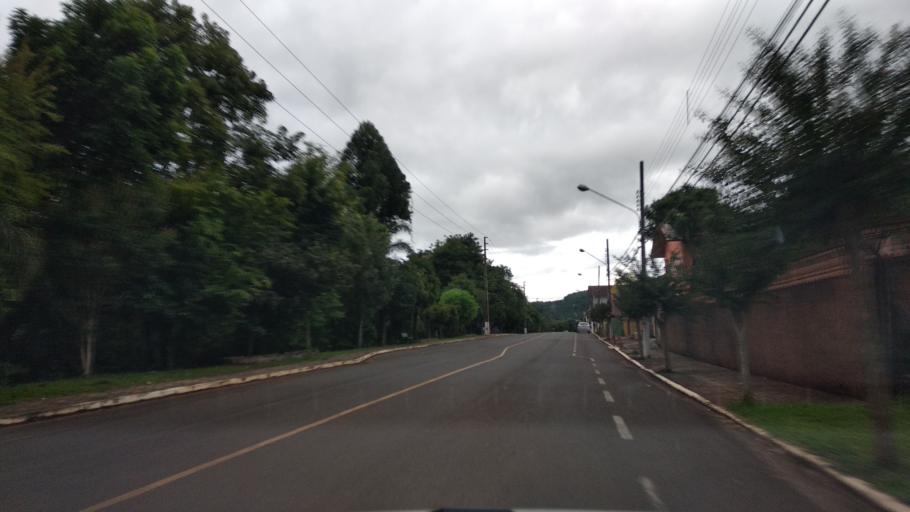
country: BR
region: Santa Catarina
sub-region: Videira
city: Videira
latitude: -27.0485
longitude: -51.2315
